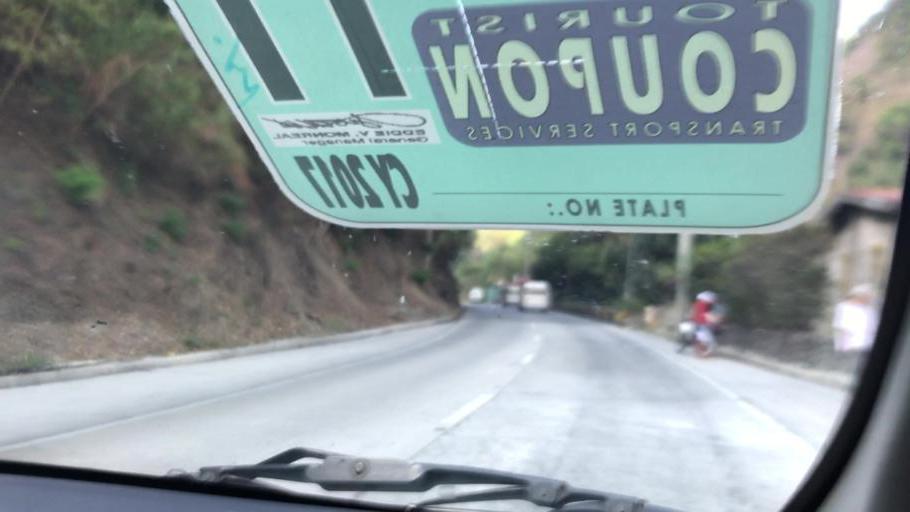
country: PH
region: Cordillera
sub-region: Province of Benguet
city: Tuba
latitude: 16.3244
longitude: 120.6145
